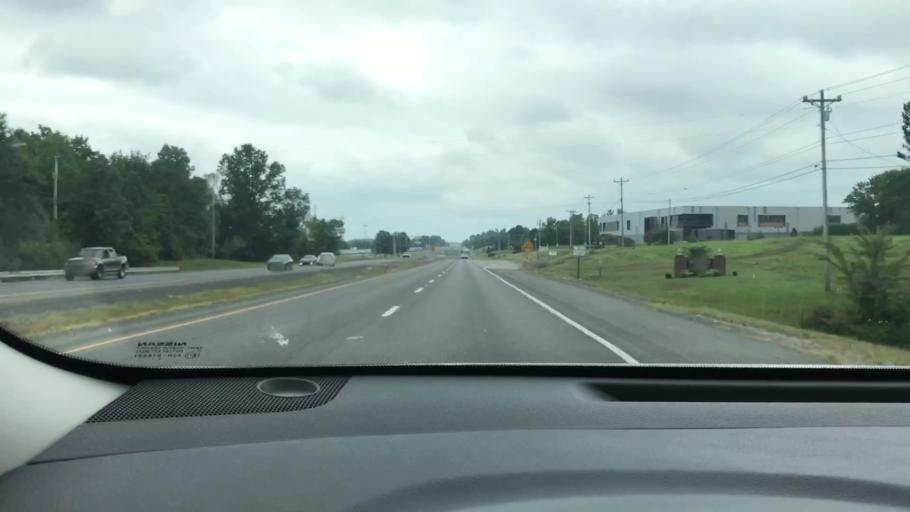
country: US
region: Kentucky
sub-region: Calloway County
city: Murray
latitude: 36.6631
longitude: -88.3052
